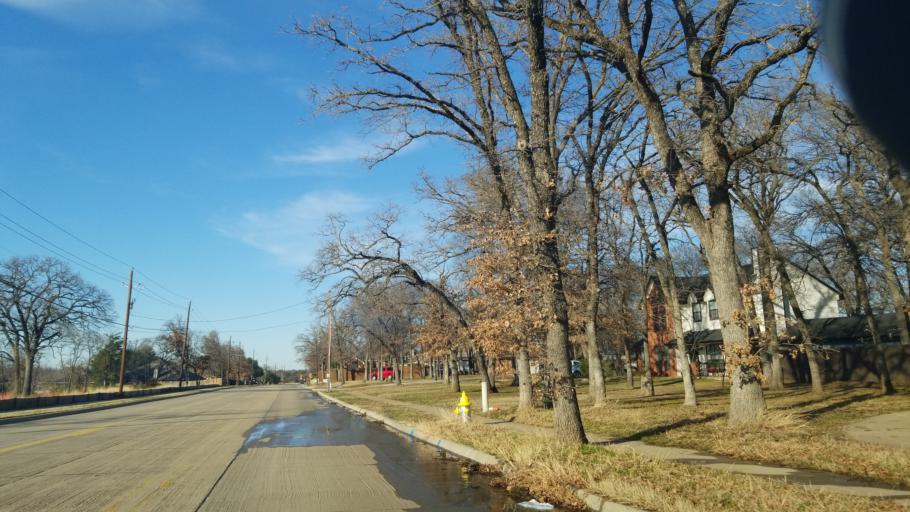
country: US
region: Texas
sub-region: Denton County
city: Corinth
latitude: 33.1389
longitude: -97.0652
